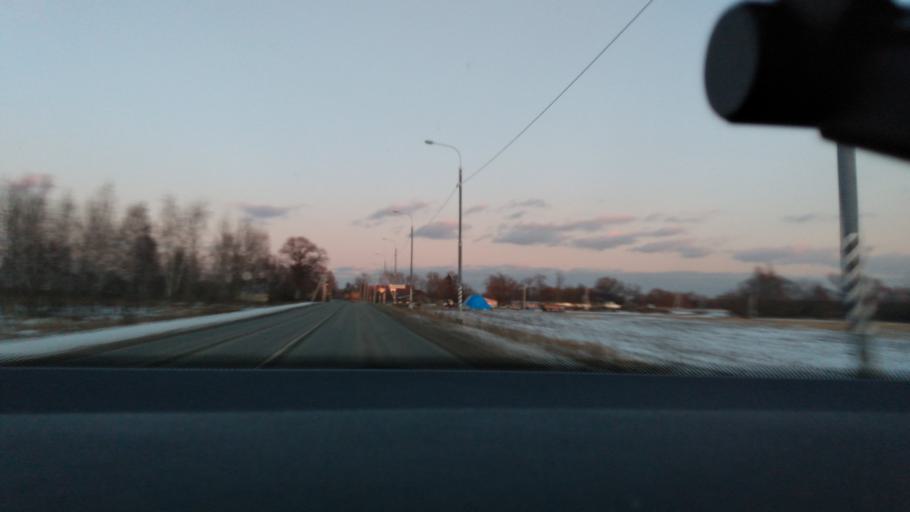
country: RU
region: Moskovskaya
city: Lukhovitsy
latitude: 55.0984
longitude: 38.9769
